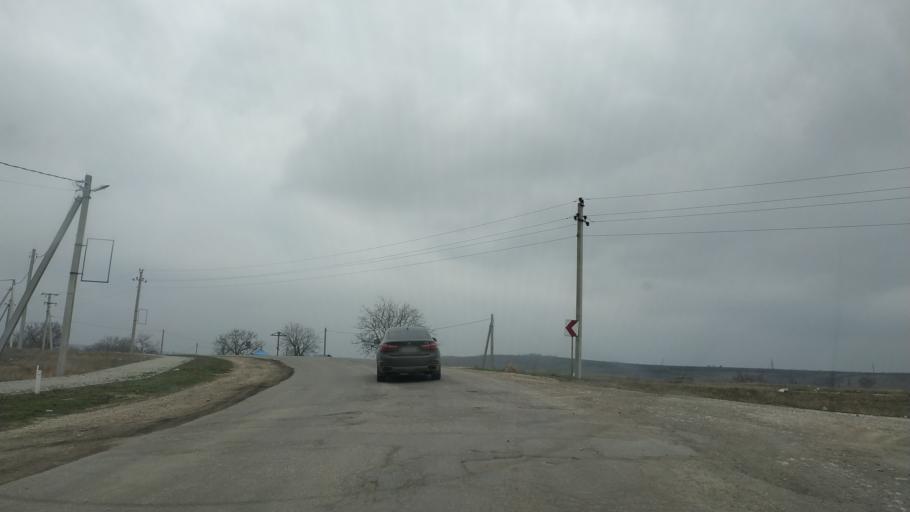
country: MD
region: Gagauzia
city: Comrat
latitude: 46.2843
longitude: 28.6749
